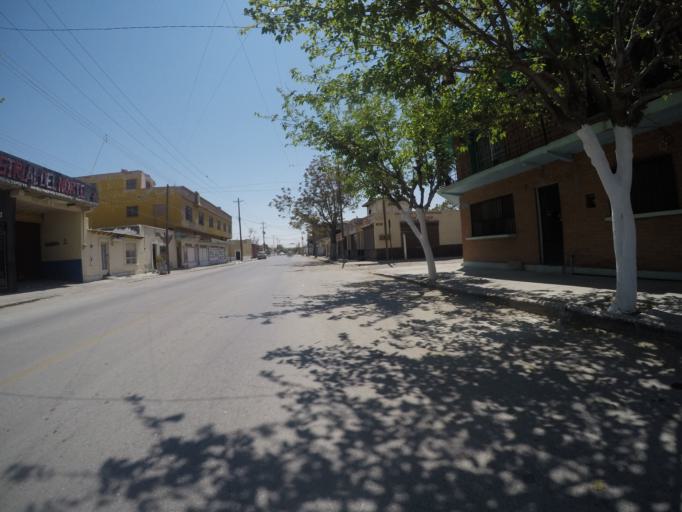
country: MX
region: Chihuahua
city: Ciudad Juarez
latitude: 31.7282
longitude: -106.4836
